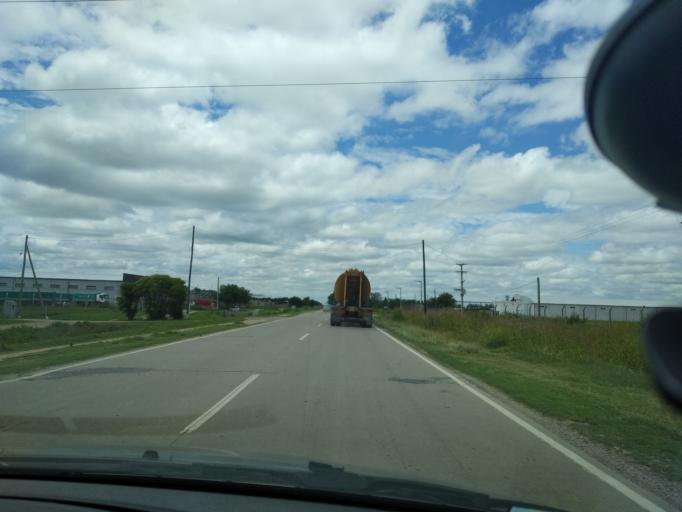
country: AR
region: Cordoba
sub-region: Departamento de Rio Segundo
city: Rio Segundo
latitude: -31.6402
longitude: -63.8943
